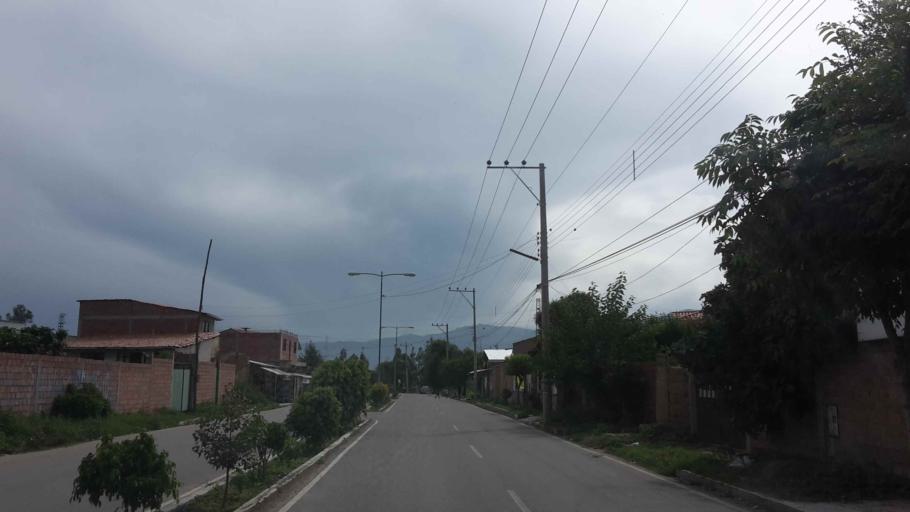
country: BO
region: Cochabamba
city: Cochabamba
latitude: -17.3328
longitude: -66.2522
